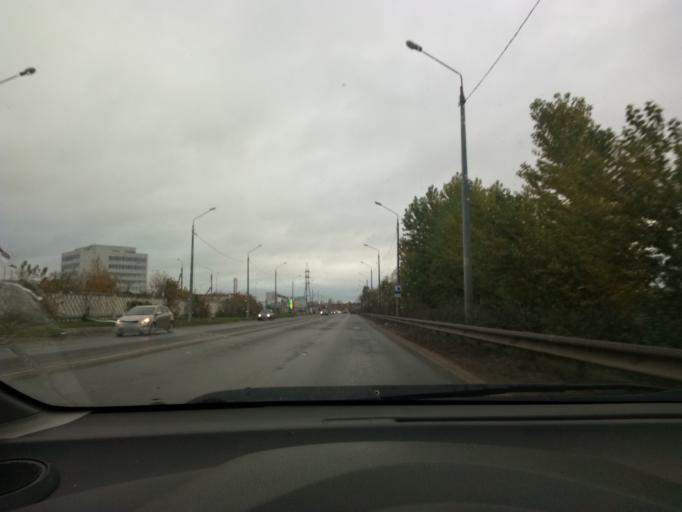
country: RU
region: Tatarstan
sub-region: Gorod Kazan'
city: Kazan
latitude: 55.8479
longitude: 49.1219
